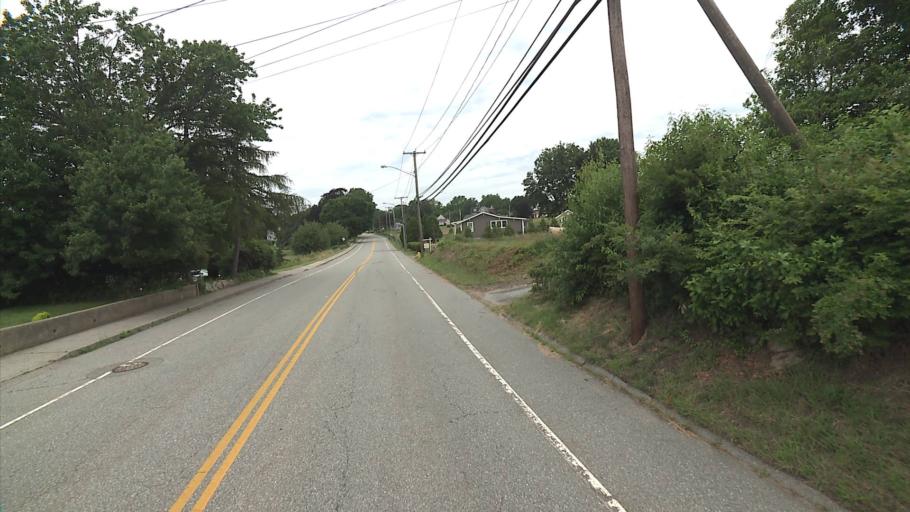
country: US
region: Connecticut
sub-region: New London County
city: Groton
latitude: 41.3243
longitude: -72.0711
